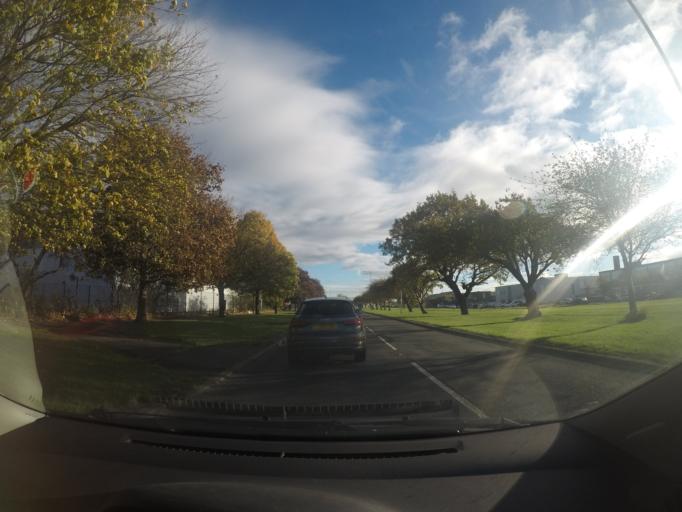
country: GB
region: England
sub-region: City and Borough of Leeds
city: Shadwell
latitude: 53.8292
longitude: -1.4607
